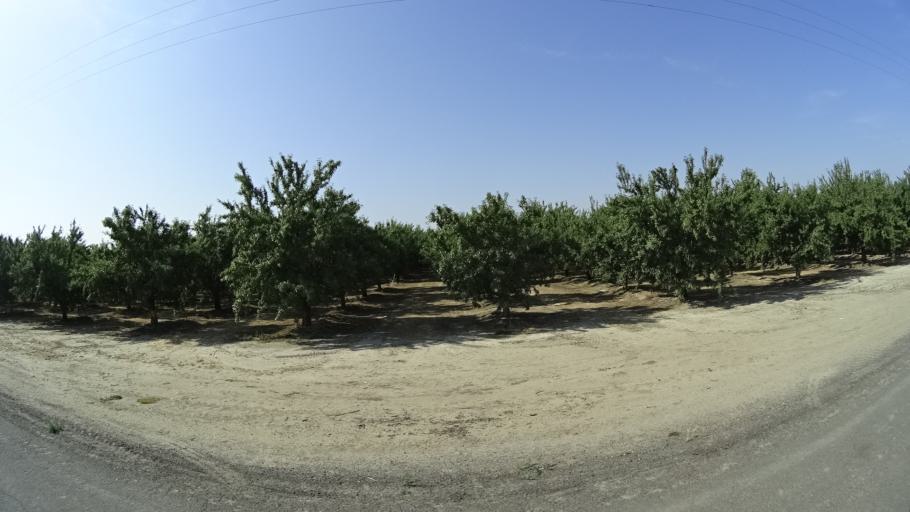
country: US
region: California
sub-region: Kings County
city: Lemoore
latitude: 36.3367
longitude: -119.8593
